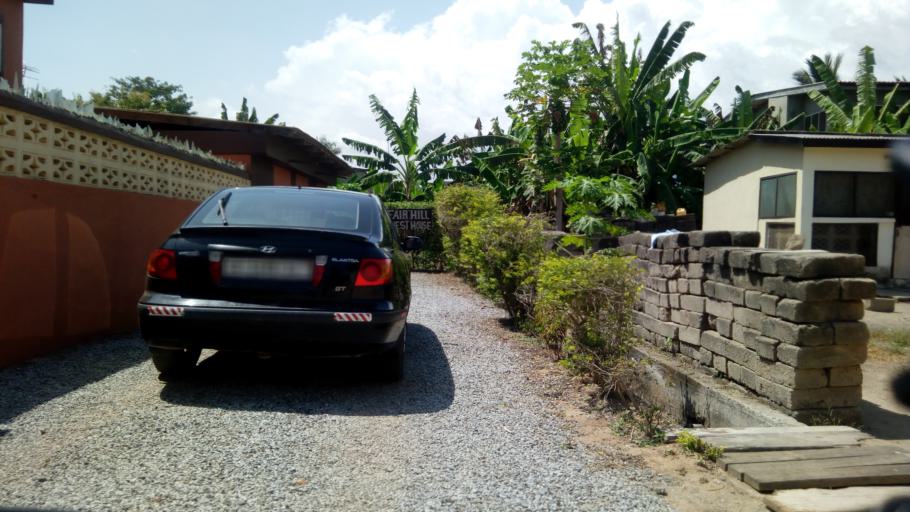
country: GH
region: Central
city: Cape Coast
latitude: 5.1302
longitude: -1.2809
